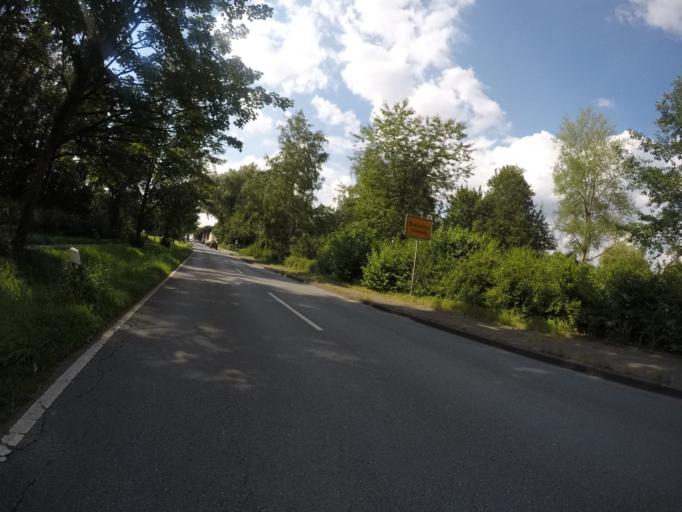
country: DE
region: North Rhine-Westphalia
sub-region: Regierungsbezirk Detmold
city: Bielefeld
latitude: 52.0540
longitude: 8.5687
